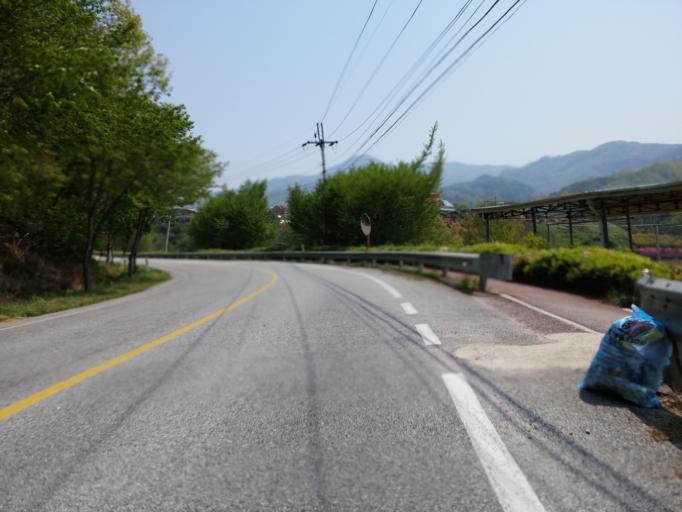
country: KR
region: Chungcheongbuk-do
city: Okcheon
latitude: 36.4429
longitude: 127.5776
